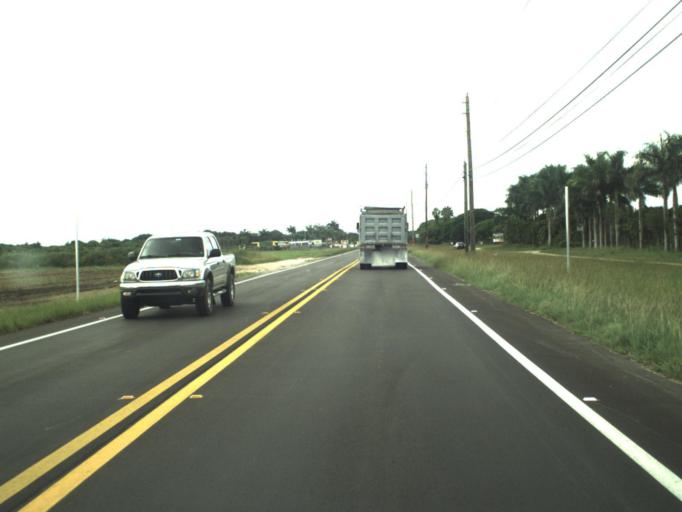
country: US
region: Florida
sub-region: Miami-Dade County
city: Country Walk
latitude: 25.6250
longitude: -80.4796
